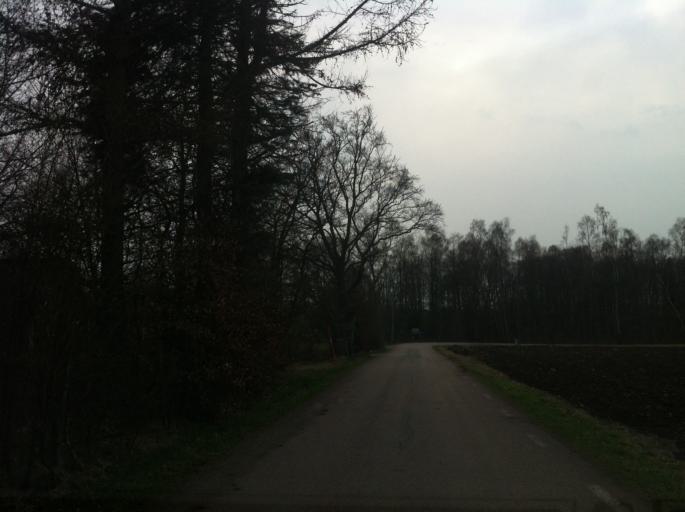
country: SE
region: Skane
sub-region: Klippans Kommun
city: Ljungbyhed
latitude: 55.9945
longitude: 13.2595
